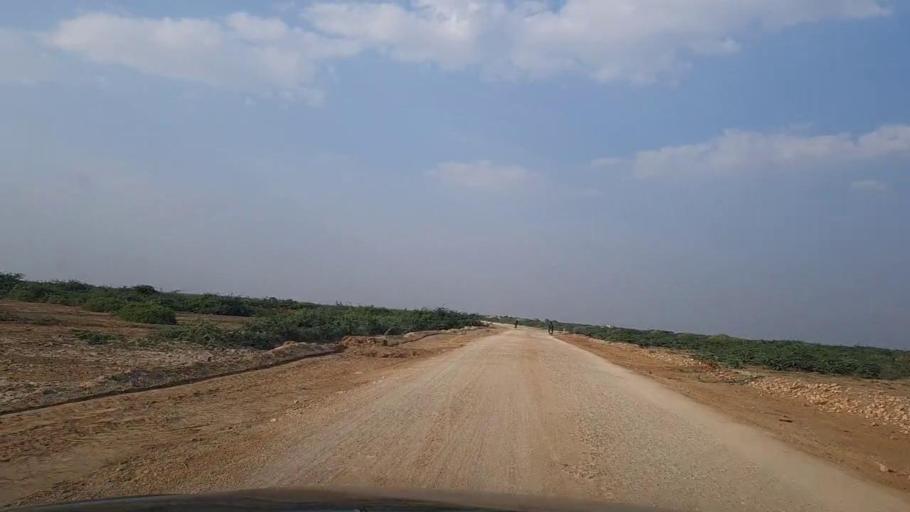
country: PK
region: Sindh
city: Gharo
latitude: 24.7932
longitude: 67.7447
